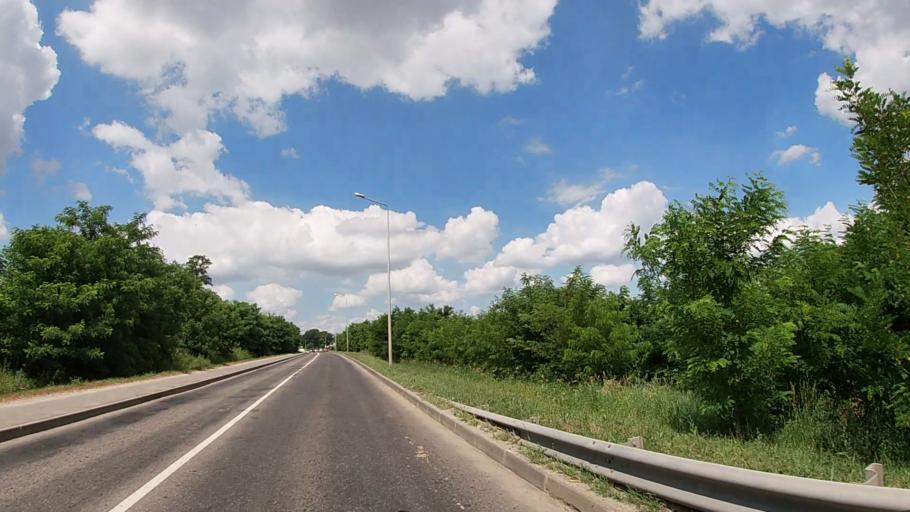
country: RU
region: Belgorod
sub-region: Belgorodskiy Rayon
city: Belgorod
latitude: 50.5942
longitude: 36.5568
